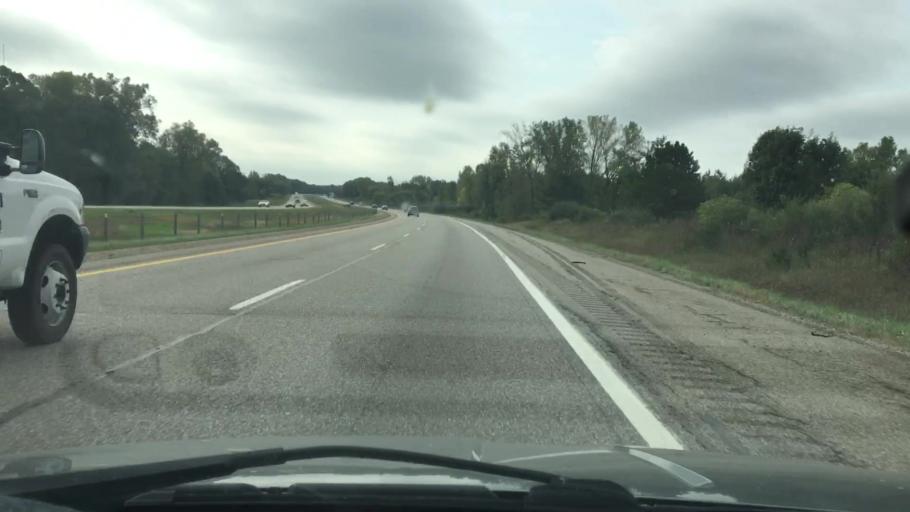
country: US
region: Michigan
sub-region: Livingston County
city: Brighton
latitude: 42.5952
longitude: -83.7410
